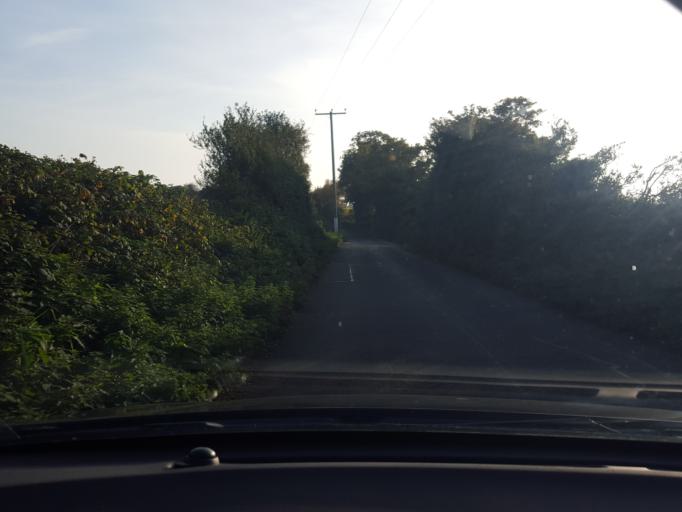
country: GB
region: England
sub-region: Essex
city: Walton-on-the-Naze
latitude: 51.8542
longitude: 1.2567
